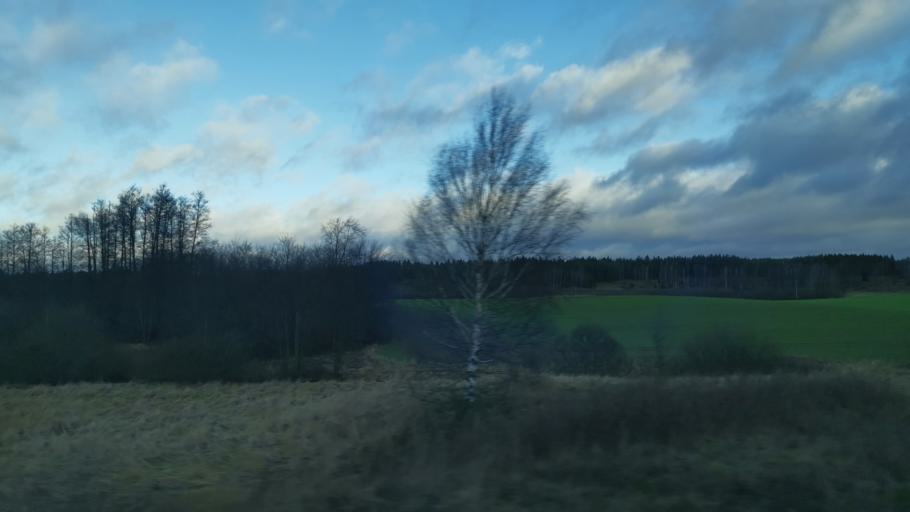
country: SE
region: Soedermanland
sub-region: Gnesta Kommun
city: Gnesta
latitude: 59.0561
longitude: 17.2768
